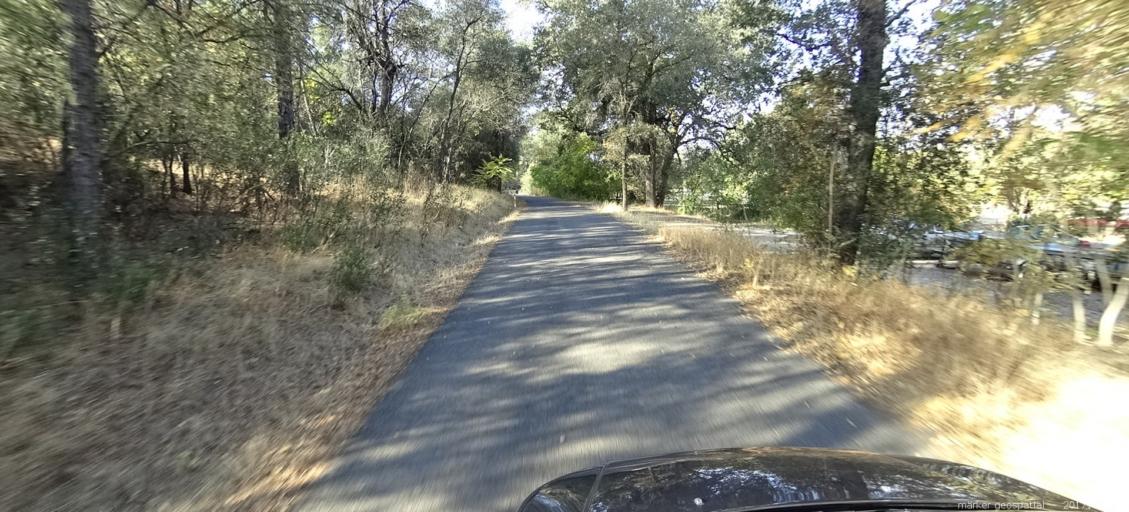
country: US
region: California
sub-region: Shasta County
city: Palo Cedro
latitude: 40.5674
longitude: -122.1418
